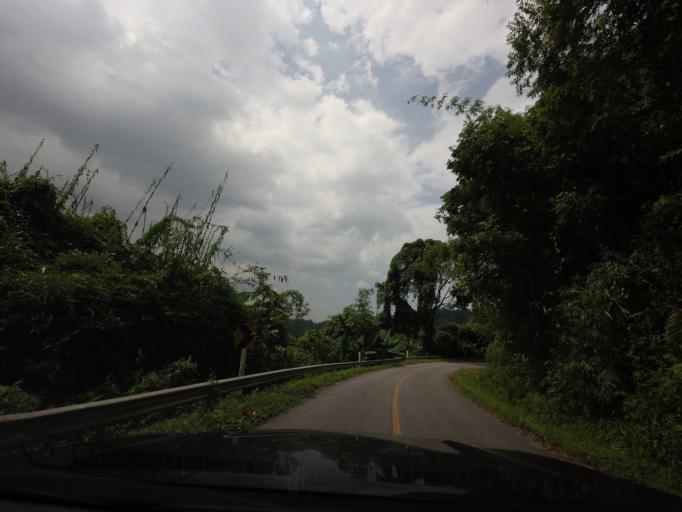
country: TH
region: Loei
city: Na Haeo
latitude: 17.7020
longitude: 100.9484
